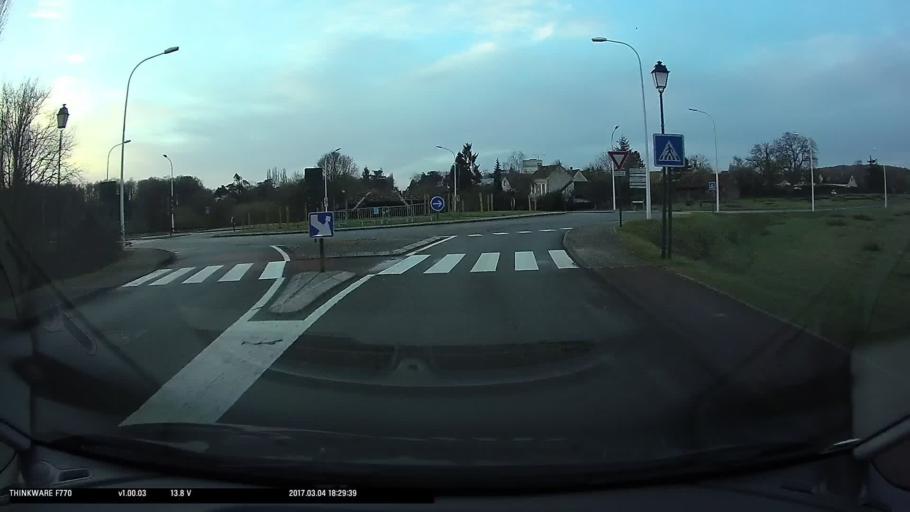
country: FR
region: Ile-de-France
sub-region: Departement du Val-d'Oise
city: Marines
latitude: 49.1376
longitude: 1.9871
